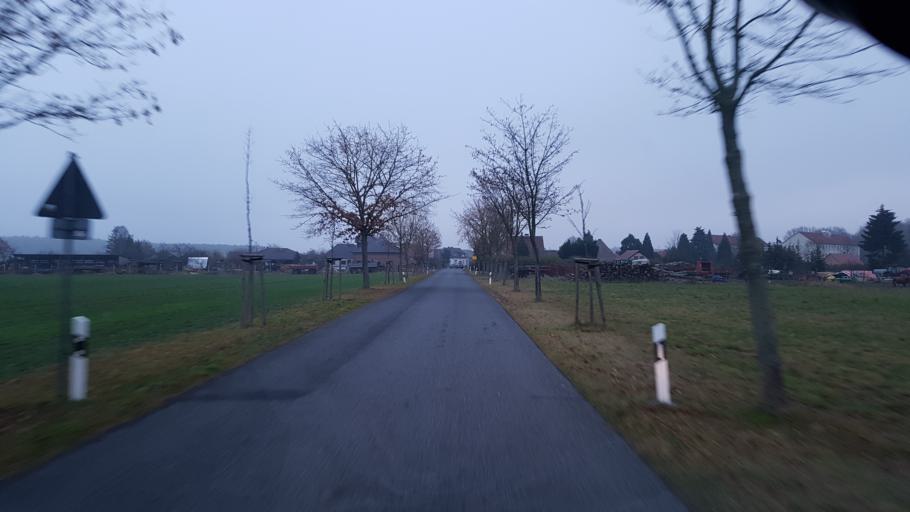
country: DE
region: Brandenburg
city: Altdobern
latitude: 51.6929
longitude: 14.0019
